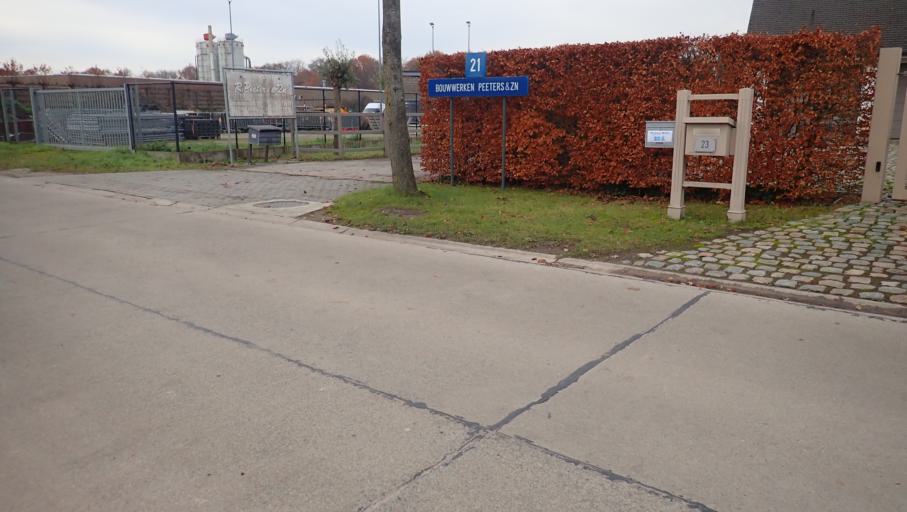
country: BE
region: Flanders
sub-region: Provincie Antwerpen
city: Hulshout
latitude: 51.0784
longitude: 4.8124
